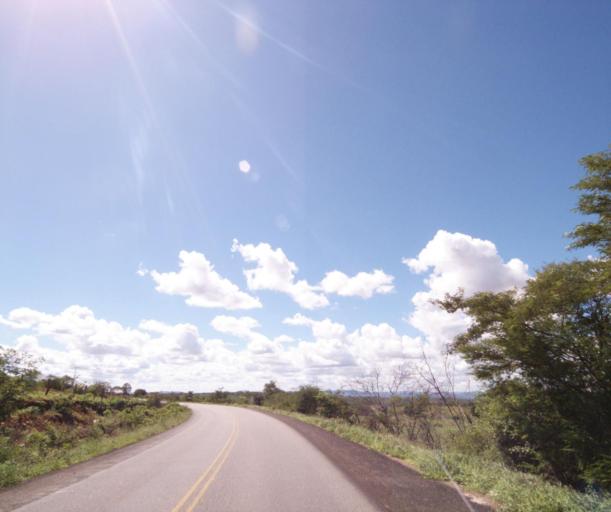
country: BR
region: Bahia
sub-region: Cacule
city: Cacule
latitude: -14.1939
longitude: -42.1431
